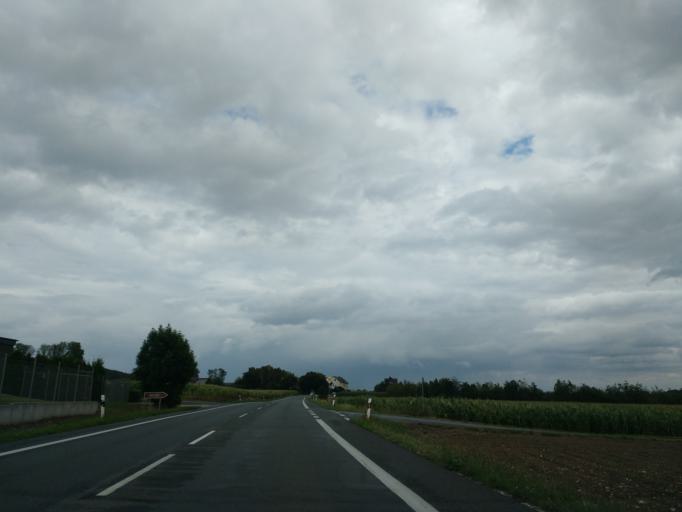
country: DE
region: Lower Saxony
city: Bad Laer
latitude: 52.1015
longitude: 8.1182
